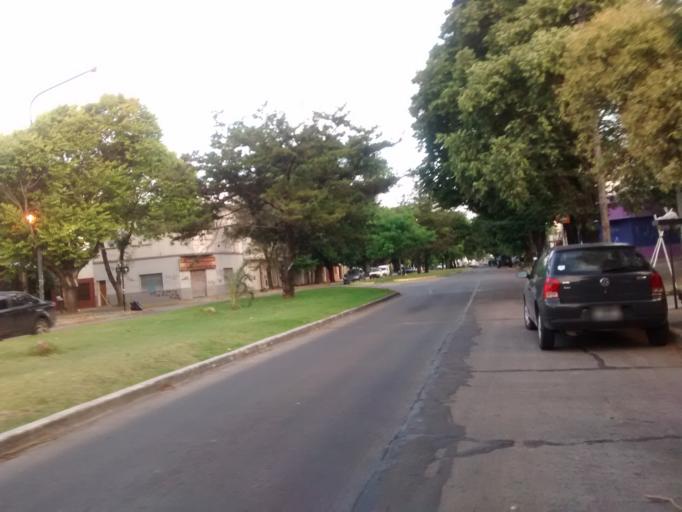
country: AR
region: Buenos Aires
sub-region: Partido de La Plata
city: La Plata
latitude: -34.9395
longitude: -57.9442
